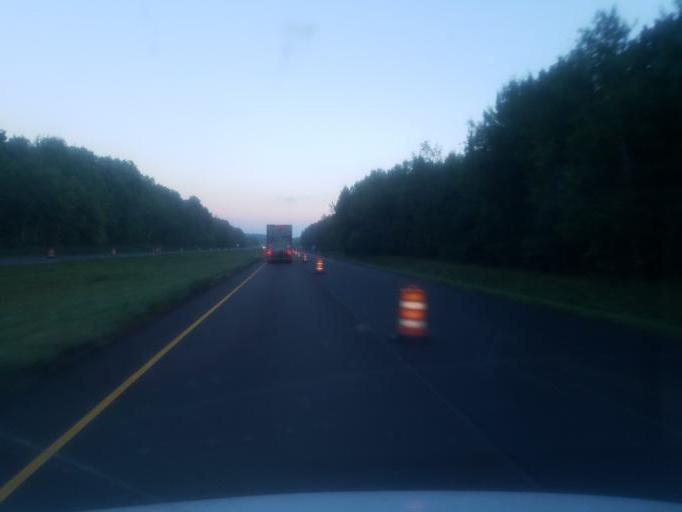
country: US
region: Ohio
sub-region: Ashtabula County
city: Jefferson
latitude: 41.7756
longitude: -80.7283
